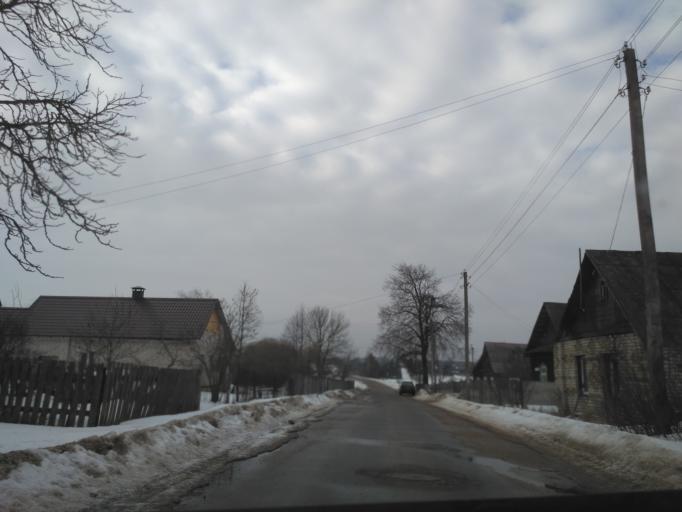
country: BY
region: Minsk
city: Zamostochcha
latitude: 53.8908
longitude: 27.9169
